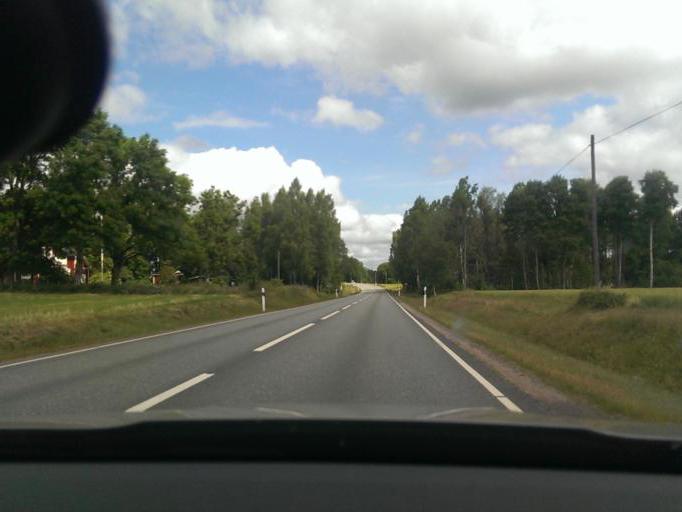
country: SE
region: Joenkoeping
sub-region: Varnamo Kommun
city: Varnamo
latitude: 57.2336
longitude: 14.0058
